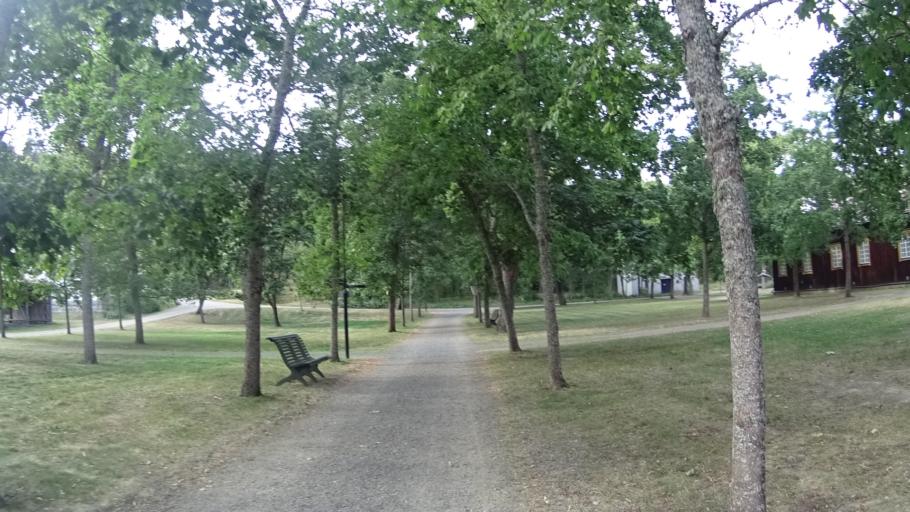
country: FI
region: Pirkanmaa
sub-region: Etelae-Pirkanmaa
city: Valkeakoski
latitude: 61.2037
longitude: 24.0617
